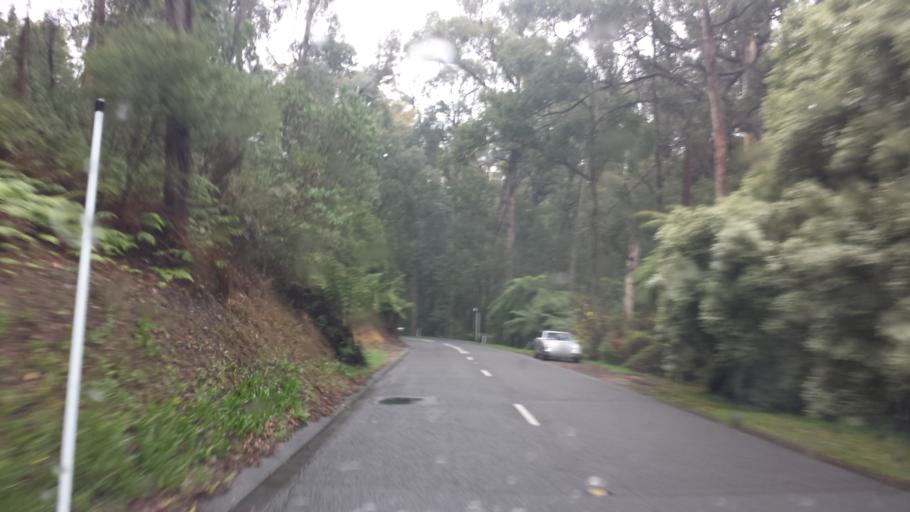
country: AU
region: Victoria
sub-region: Yarra Ranges
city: Monbulk
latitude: -37.8791
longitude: 145.4061
